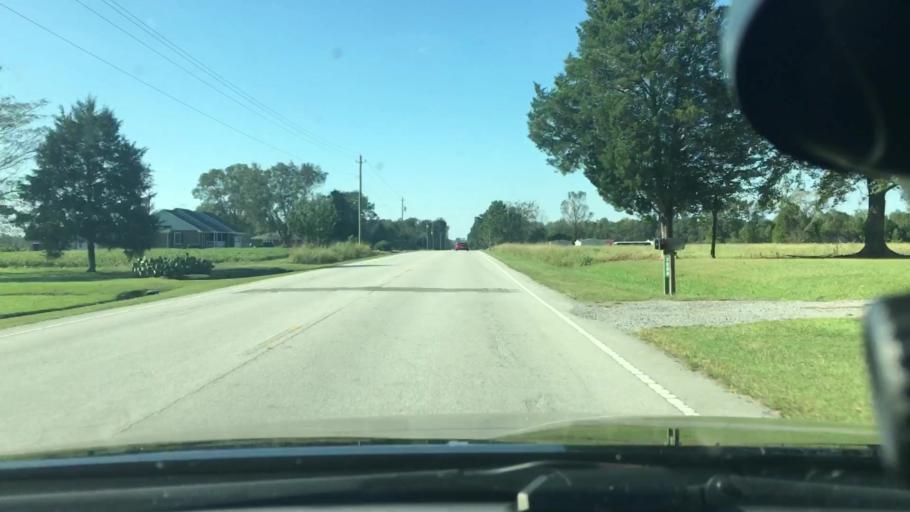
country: US
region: North Carolina
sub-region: Craven County
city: Vanceboro
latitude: 35.3629
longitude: -77.1994
